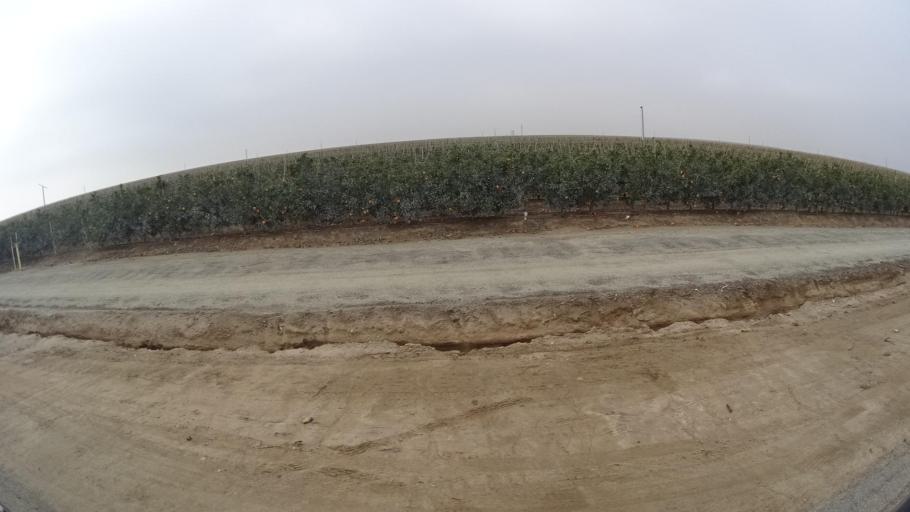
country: US
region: California
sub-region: Kern County
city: Maricopa
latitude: 35.0731
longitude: -119.3138
